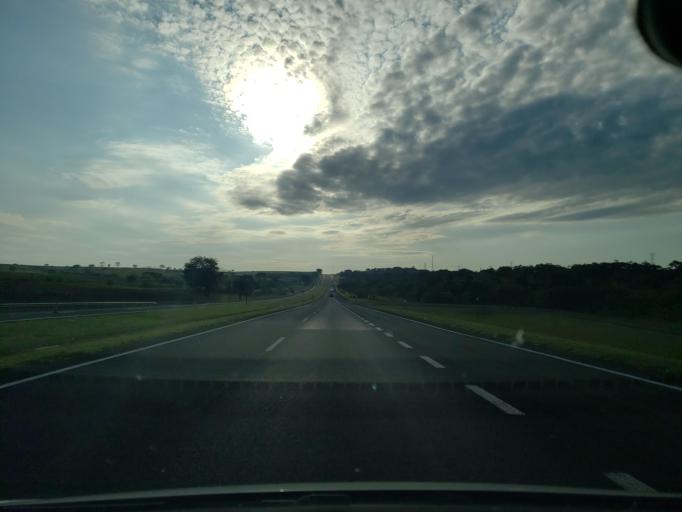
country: BR
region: Sao Paulo
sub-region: Valparaiso
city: Valparaiso
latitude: -21.1684
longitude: -50.9362
